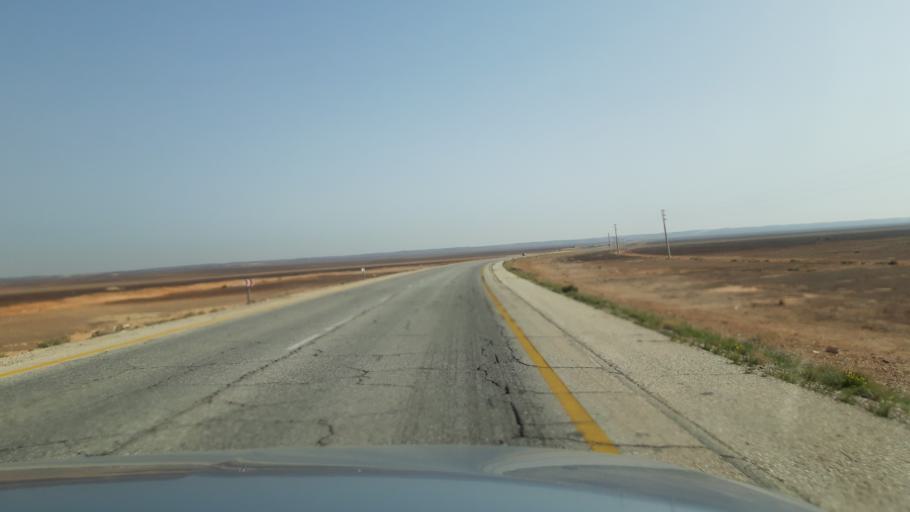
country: JO
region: Amman
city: Al Azraq ash Shamali
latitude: 31.8180
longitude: 36.6010
